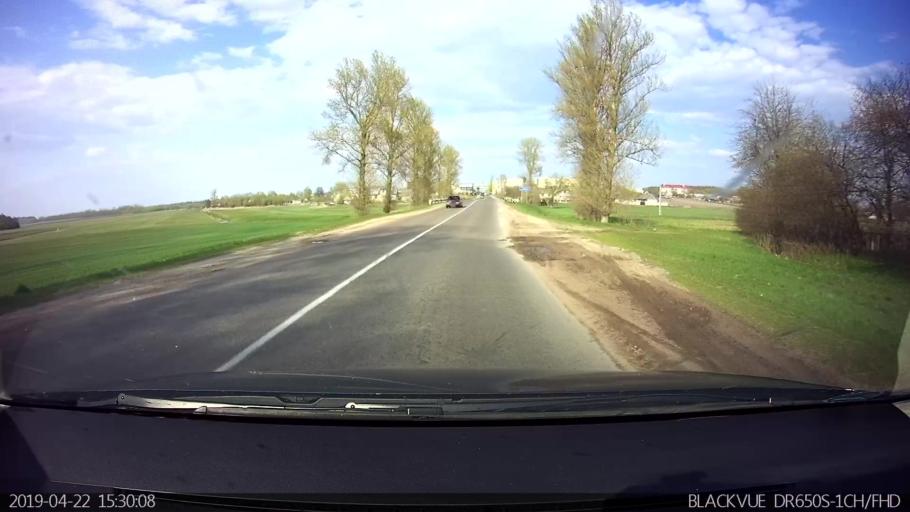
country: BY
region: Brest
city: Vysokaye
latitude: 52.3955
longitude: 23.3757
